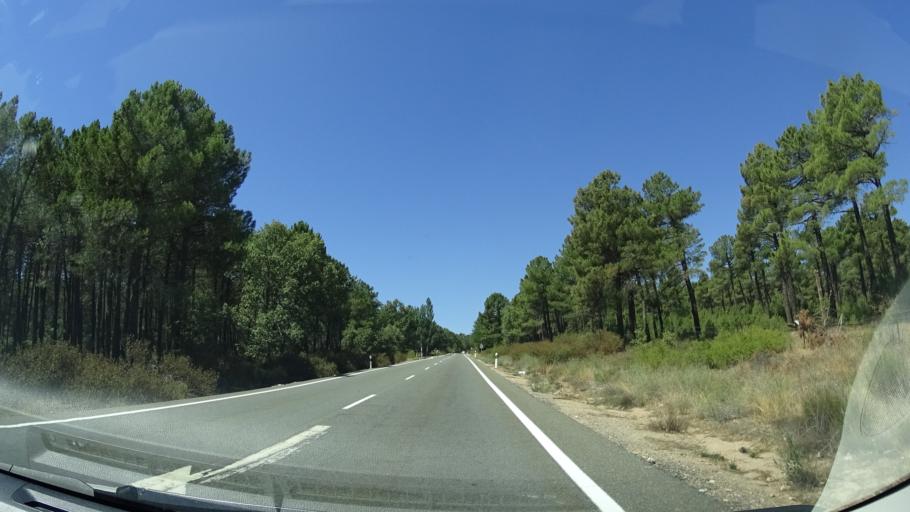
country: ES
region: Castille and Leon
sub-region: Provincia de Avila
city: Navalperal de Pinares
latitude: 40.5920
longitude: -4.3728
